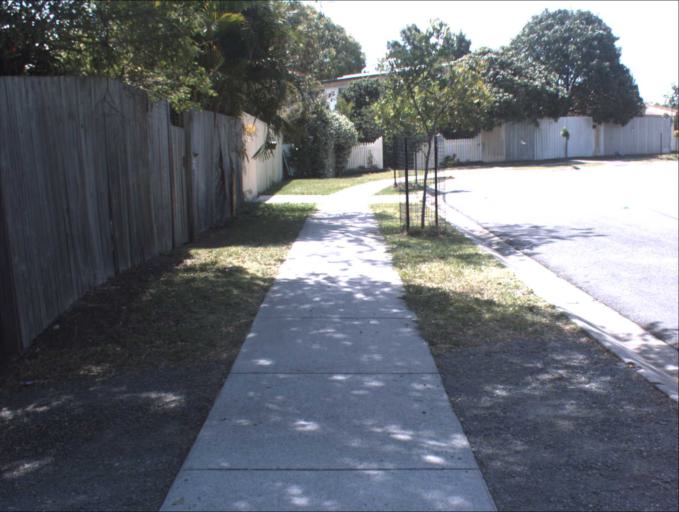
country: AU
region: Queensland
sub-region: Logan
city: Woodridge
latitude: -27.6399
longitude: 153.1016
